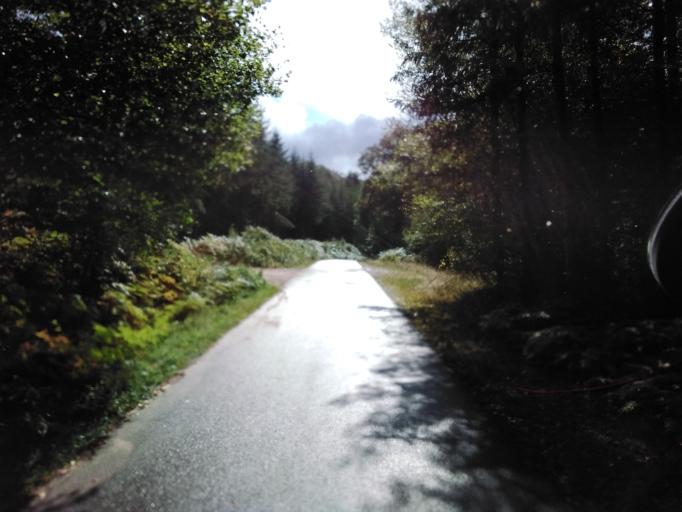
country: FR
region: Bourgogne
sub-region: Departement de la Nievre
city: Lormes
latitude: 47.3150
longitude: 3.8964
